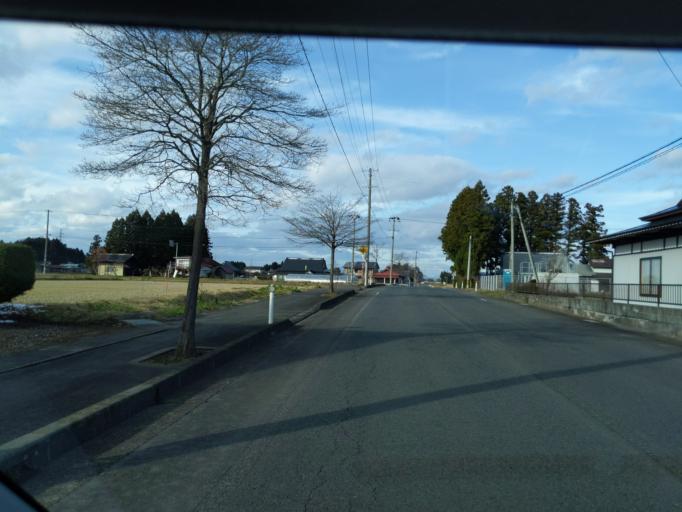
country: JP
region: Iwate
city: Mizusawa
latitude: 39.1226
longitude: 141.0923
